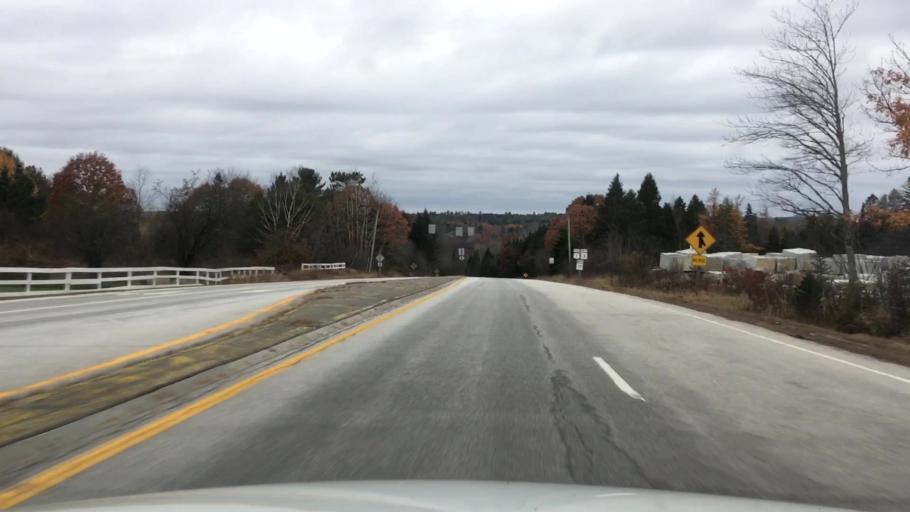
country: US
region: Maine
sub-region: Hancock County
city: Orland
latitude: 44.5742
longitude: -68.7317
